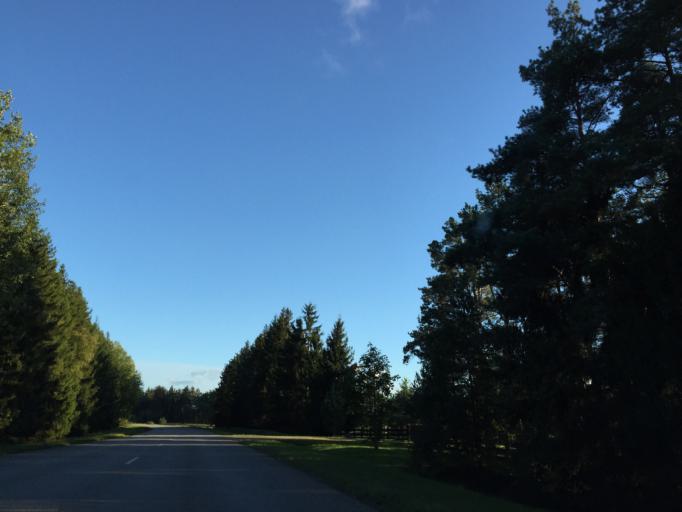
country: LV
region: Kuldigas Rajons
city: Kuldiga
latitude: 56.9162
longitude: 22.0549
